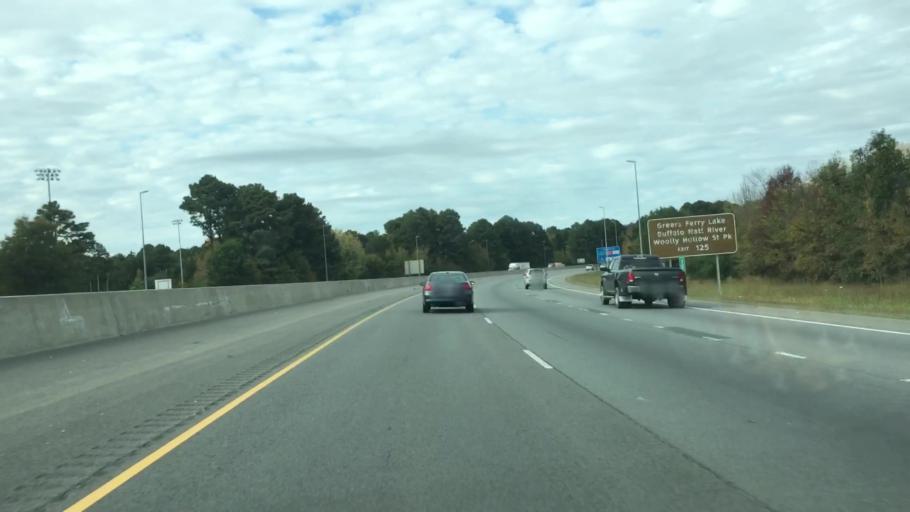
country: US
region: Arkansas
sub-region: Faulkner County
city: Conway
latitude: 35.1003
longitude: -92.4307
